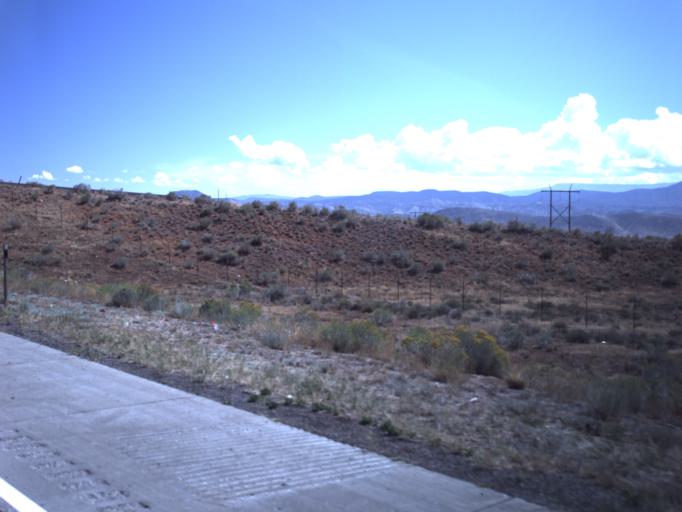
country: US
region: Utah
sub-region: Sevier County
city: Aurora
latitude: 38.8473
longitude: -112.0083
